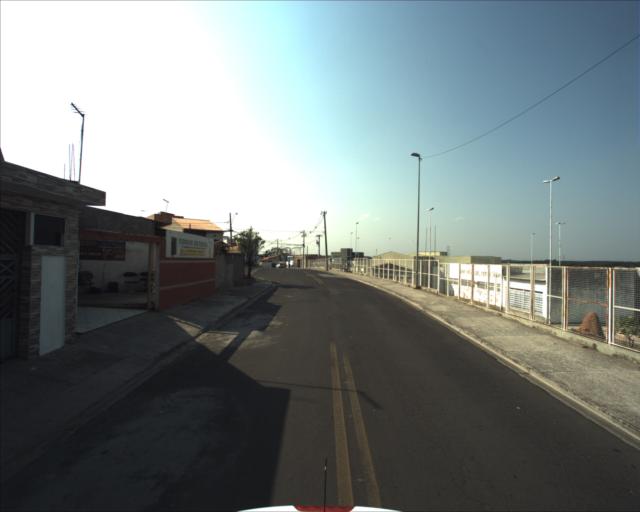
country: BR
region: Sao Paulo
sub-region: Sorocaba
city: Sorocaba
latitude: -23.4254
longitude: -47.4653
